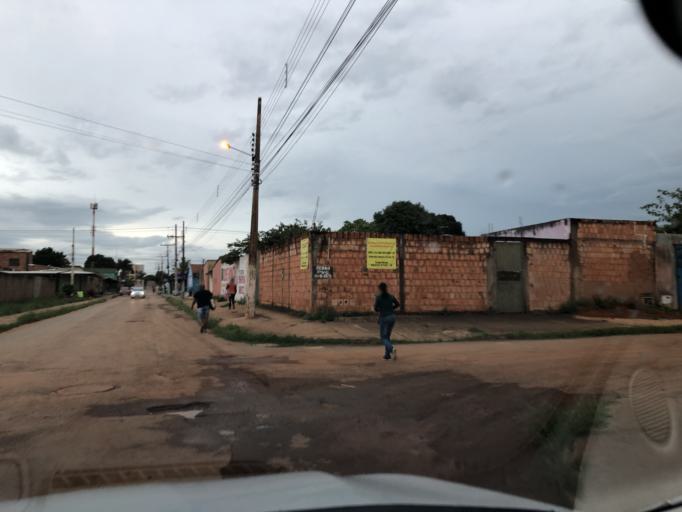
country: BR
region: Goias
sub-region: Luziania
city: Luziania
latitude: -16.1106
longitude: -47.9721
